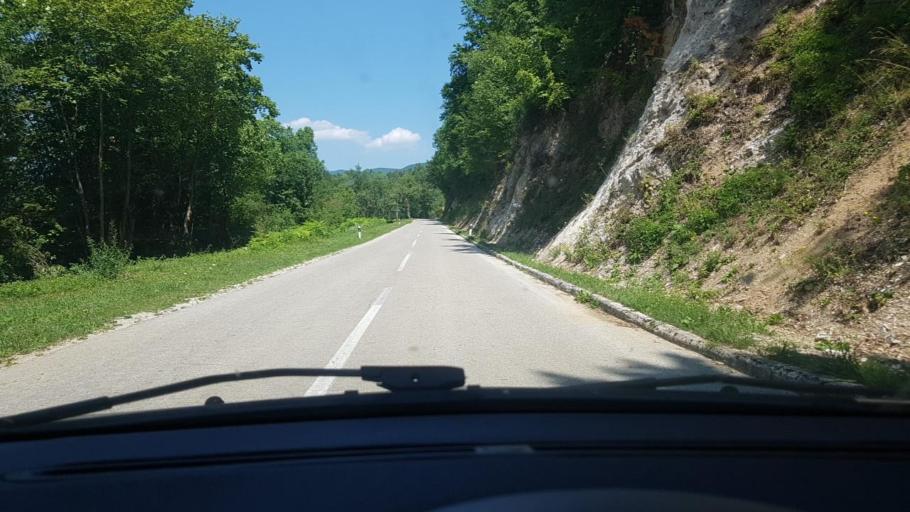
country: BA
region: Federation of Bosnia and Herzegovina
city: Orasac
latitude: 44.5886
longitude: 16.0822
